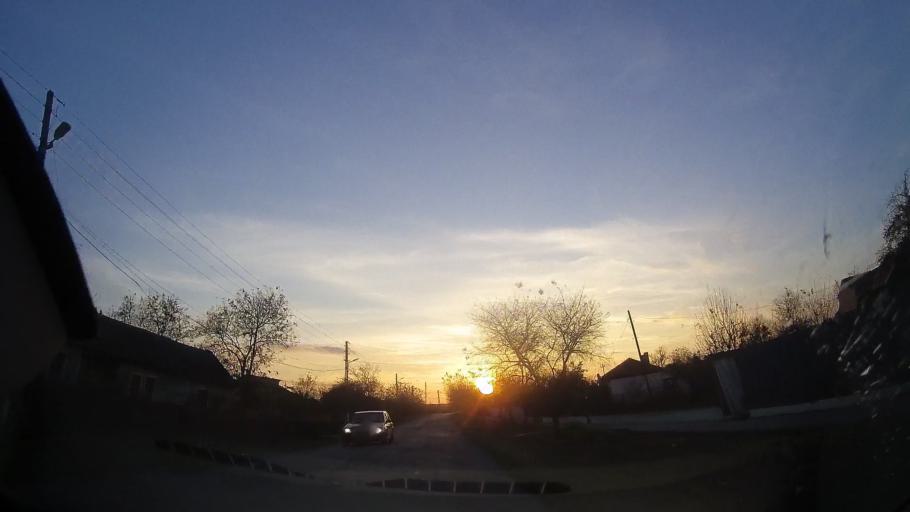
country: RO
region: Constanta
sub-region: Comuna Mereni
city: Mereni
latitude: 44.0308
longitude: 28.3792
